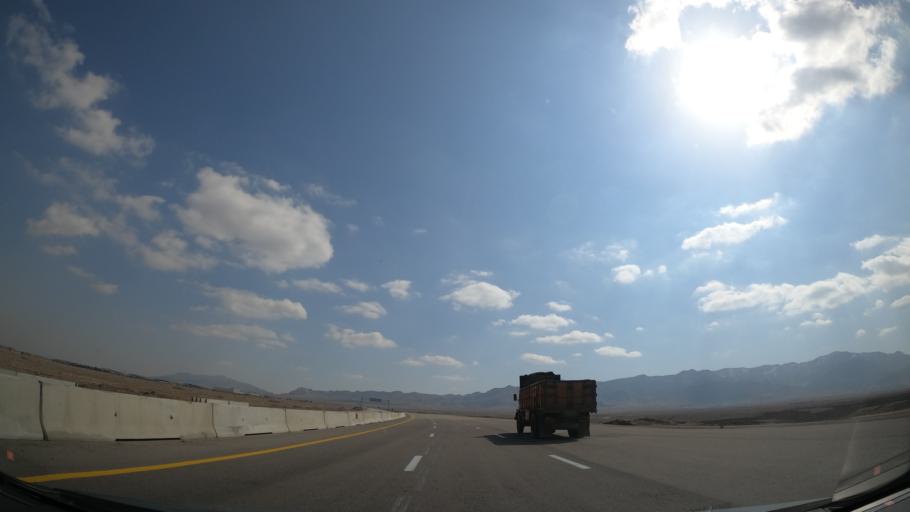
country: IR
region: Alborz
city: Eshtehard
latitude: 35.7270
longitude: 50.5629
